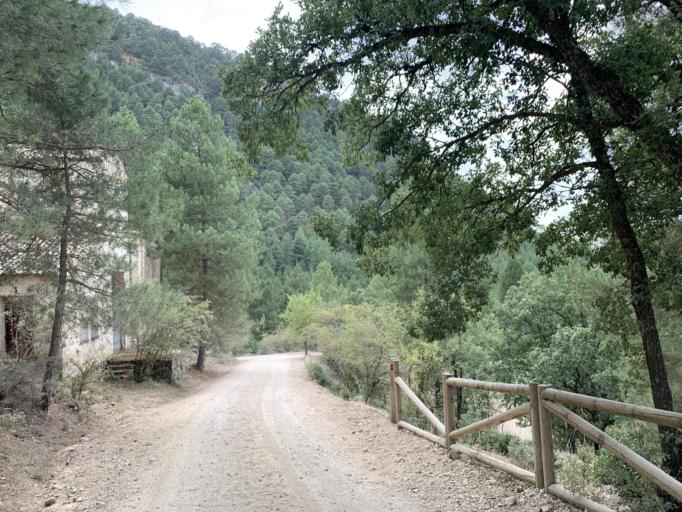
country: ES
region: Castille-La Mancha
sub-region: Provincia de Guadalajara
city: Taravilla
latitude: 40.6485
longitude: -1.9787
